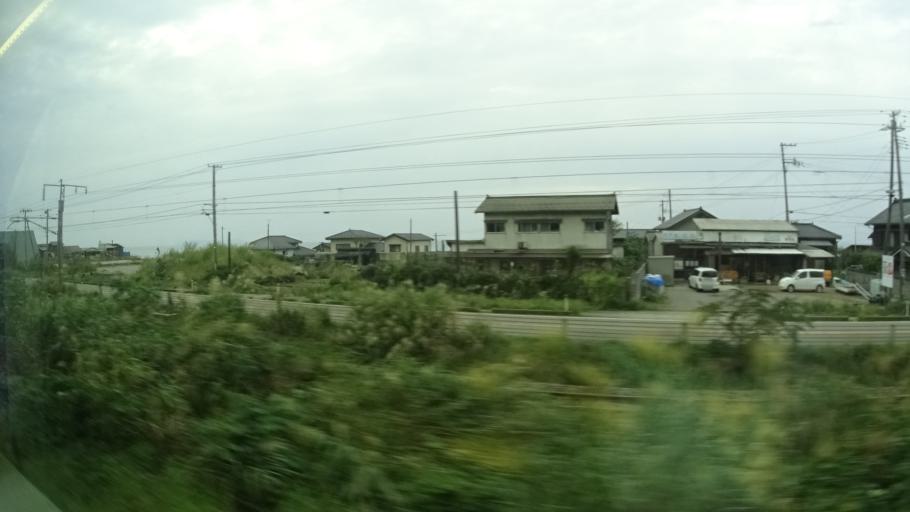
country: JP
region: Niigata
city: Murakami
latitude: 38.5377
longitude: 139.5488
